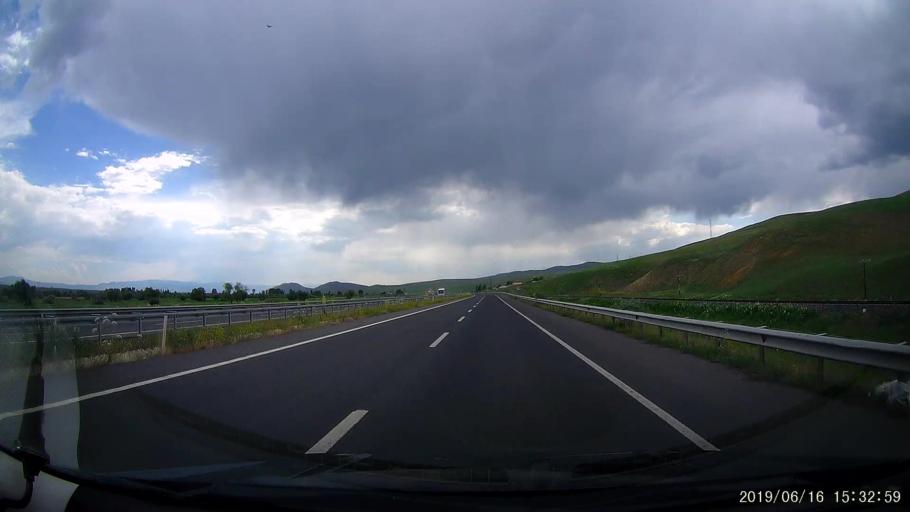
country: TR
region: Erzurum
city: Horasan
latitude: 40.0294
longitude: 42.0325
